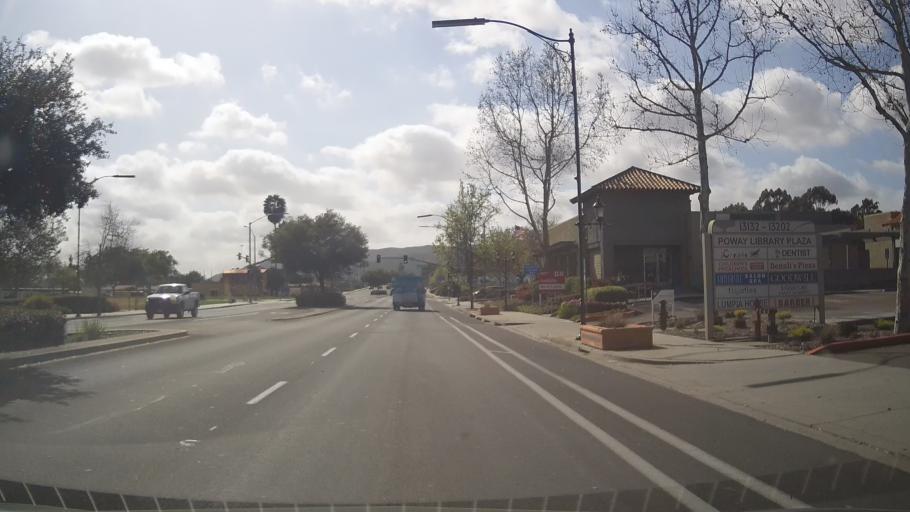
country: US
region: California
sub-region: San Diego County
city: Poway
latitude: 32.9566
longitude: -117.0455
